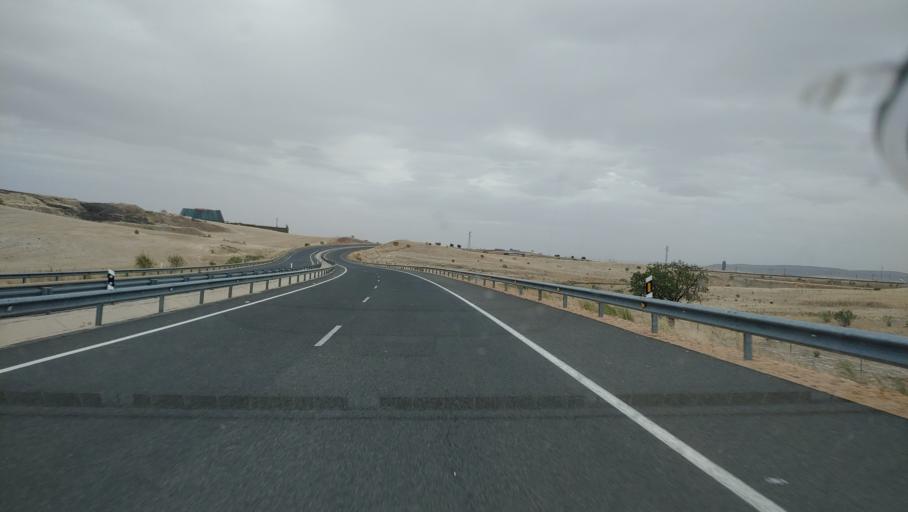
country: ES
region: Castille-La Mancha
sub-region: Provincia de Ciudad Real
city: Canada de Calatrava
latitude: 38.8739
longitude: -4.0031
